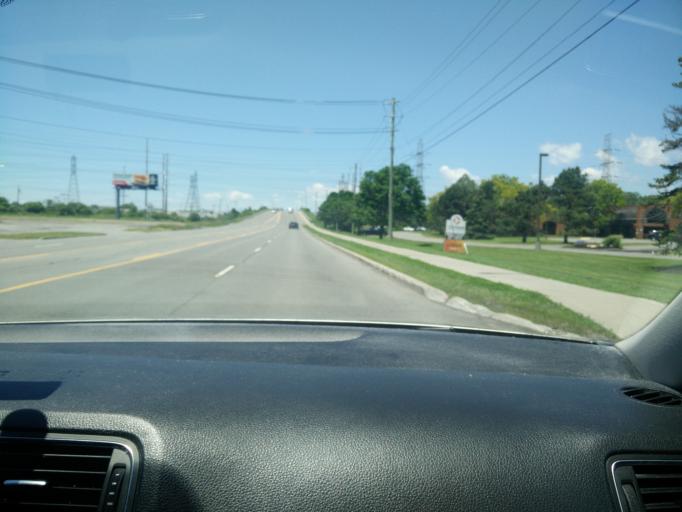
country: US
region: New York
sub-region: Erie County
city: West Seneca
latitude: 42.8318
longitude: -78.7782
